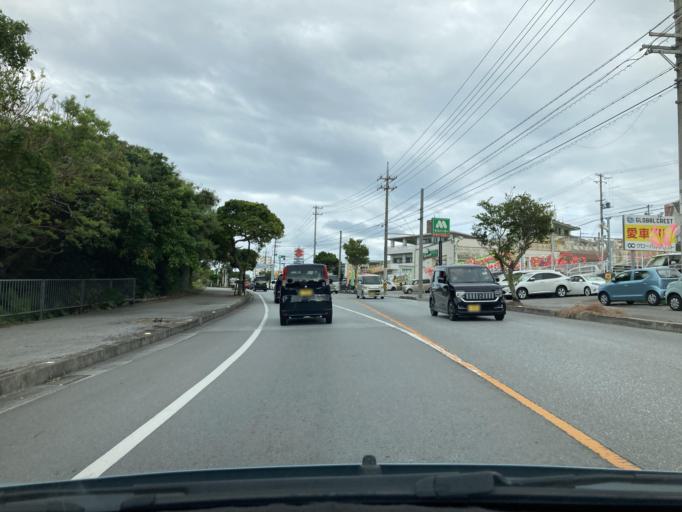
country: JP
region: Okinawa
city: Ginowan
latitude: 26.2452
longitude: 127.7615
